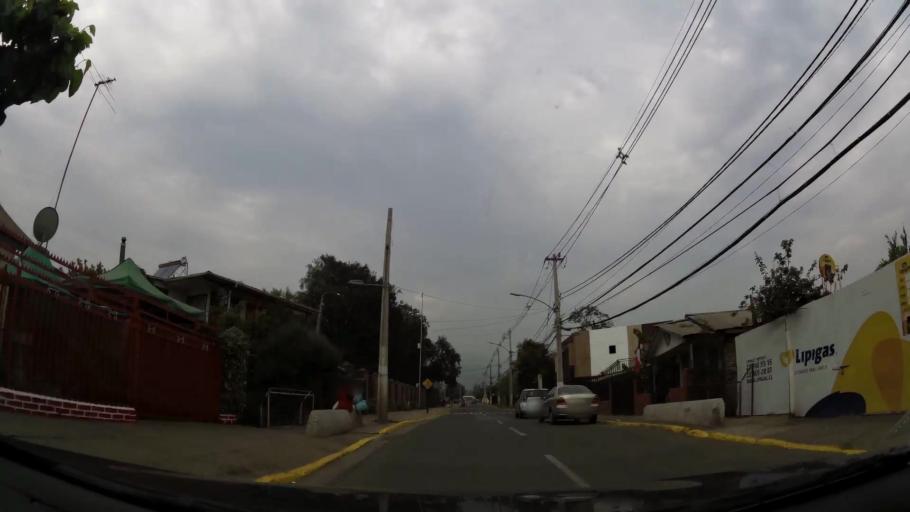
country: CL
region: Santiago Metropolitan
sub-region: Provincia de Chacabuco
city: Chicureo Abajo
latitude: -33.2063
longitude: -70.6722
